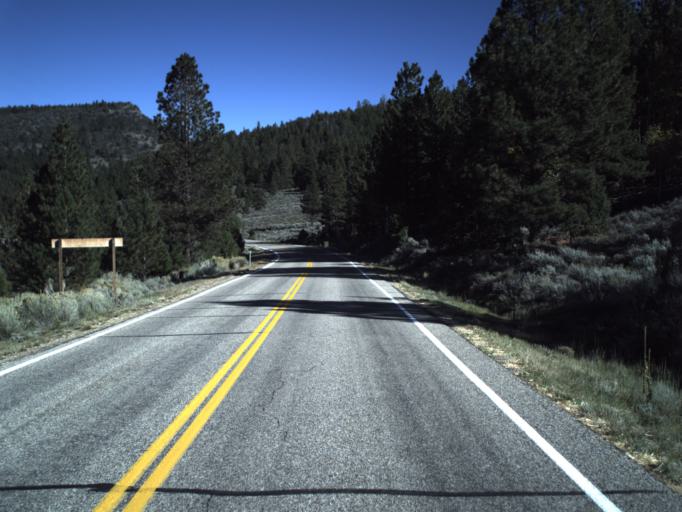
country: US
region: Utah
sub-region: Garfield County
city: Panguitch
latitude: 37.7228
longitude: -112.6218
